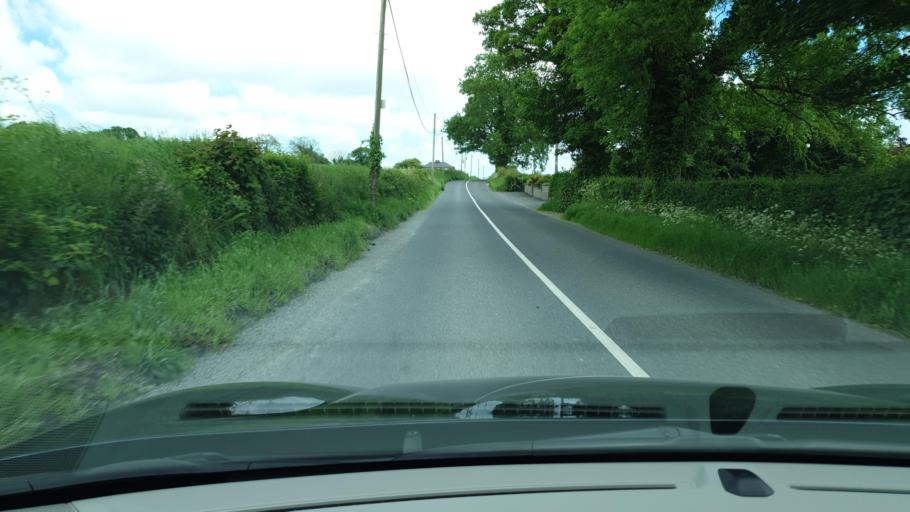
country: IE
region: Leinster
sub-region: An Mhi
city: Slane
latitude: 53.7810
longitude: -6.6313
